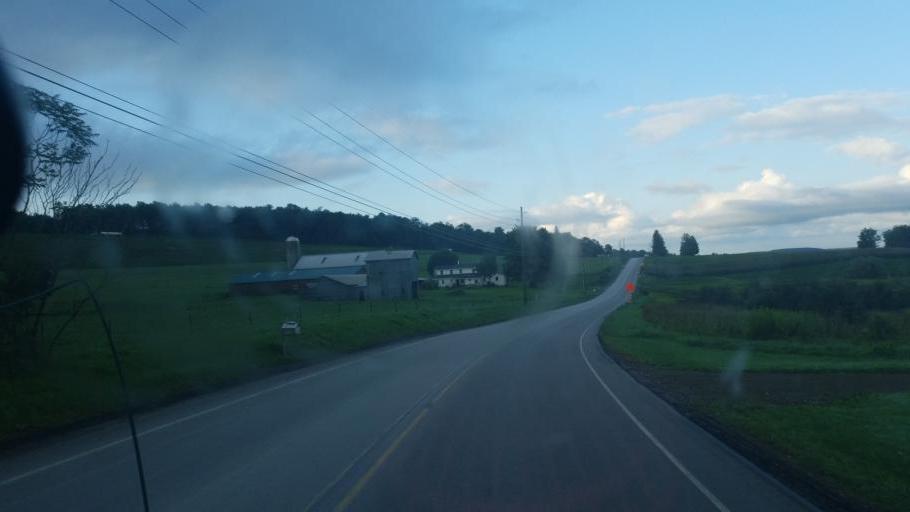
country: US
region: Pennsylvania
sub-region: Potter County
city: Galeton
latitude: 41.8558
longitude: -77.7673
